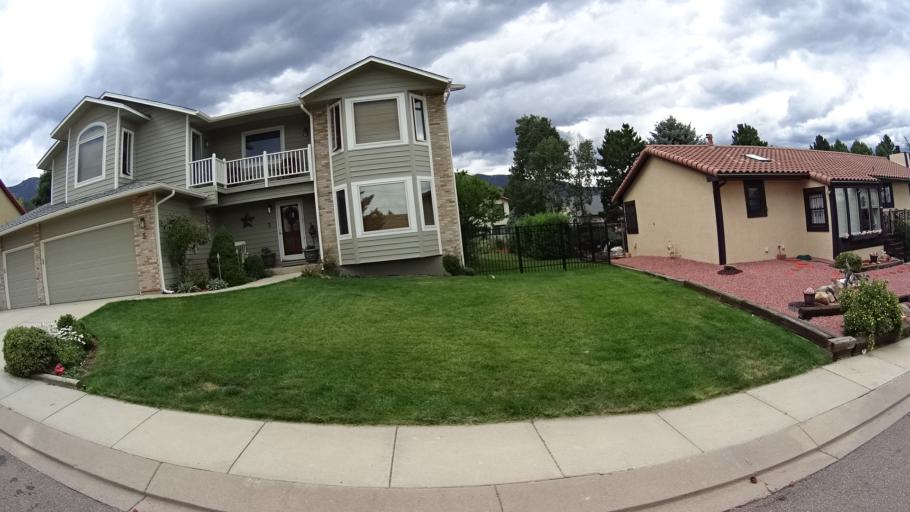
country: US
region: Colorado
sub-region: El Paso County
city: Manitou Springs
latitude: 38.8442
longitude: -104.8969
